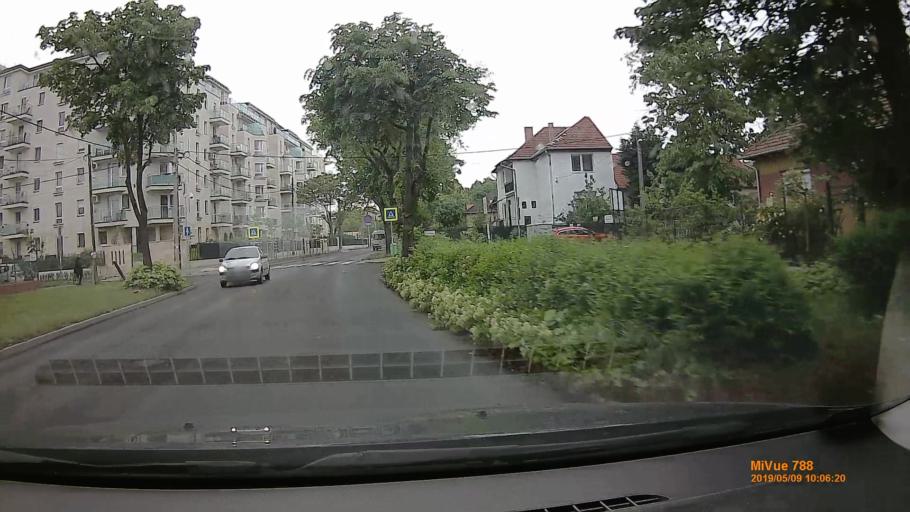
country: HU
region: Budapest
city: Budapest XIV. keruelet
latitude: 47.5337
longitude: 19.1078
